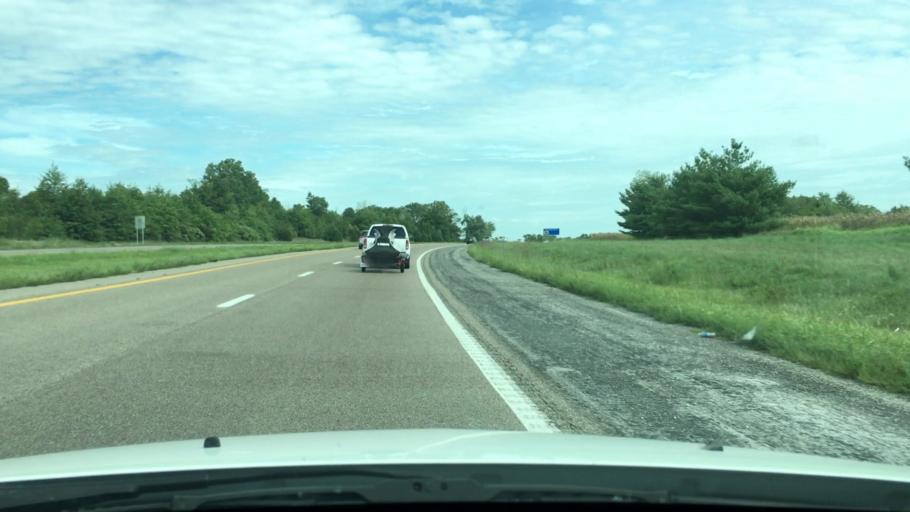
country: US
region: Missouri
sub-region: Audrain County
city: Mexico
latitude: 39.0076
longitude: -91.8928
